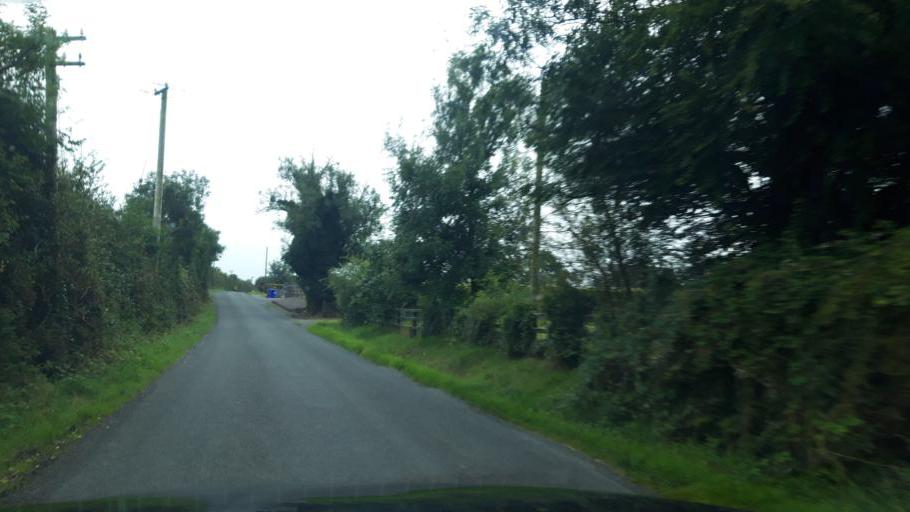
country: IE
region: Leinster
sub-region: Kilkenny
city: Ballyragget
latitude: 52.6888
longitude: -7.4239
